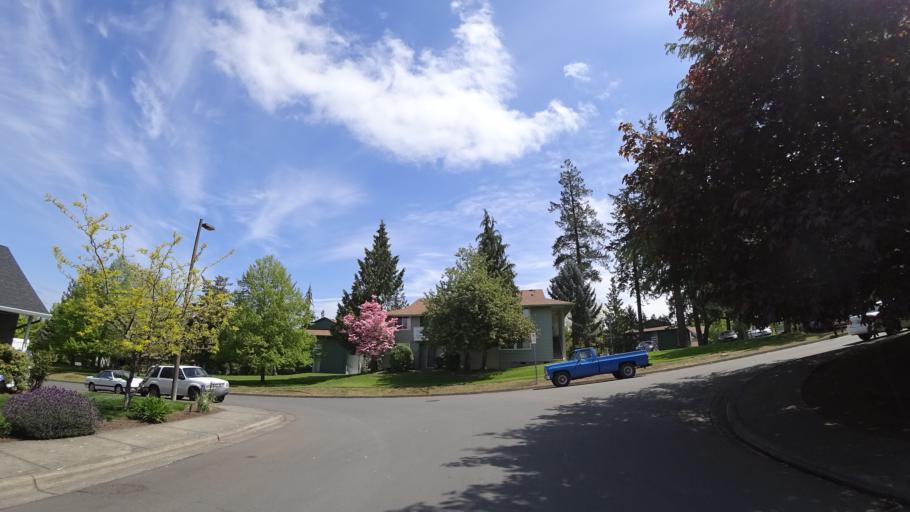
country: US
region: Oregon
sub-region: Washington County
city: Aloha
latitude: 45.4668
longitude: -122.8883
